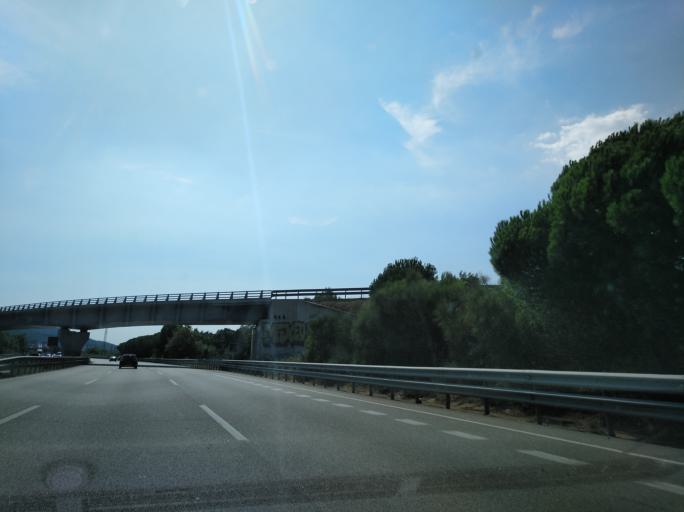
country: ES
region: Catalonia
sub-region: Provincia de Barcelona
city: Llinars del Valles
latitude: 41.6458
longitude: 2.4216
